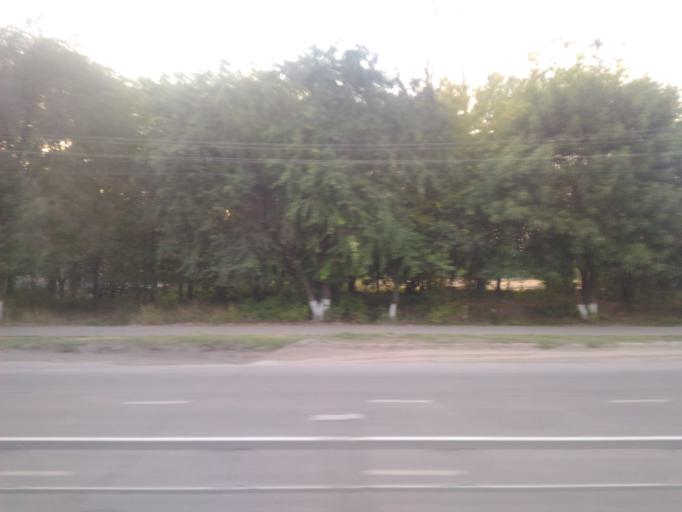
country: RU
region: Ulyanovsk
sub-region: Ulyanovskiy Rayon
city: Ulyanovsk
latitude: 54.2843
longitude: 48.3007
